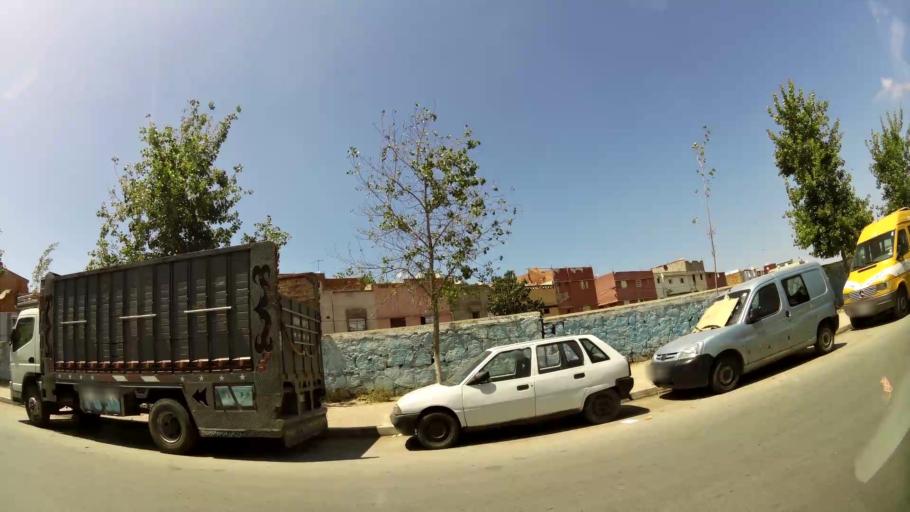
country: MA
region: Gharb-Chrarda-Beni Hssen
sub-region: Kenitra Province
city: Kenitra
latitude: 34.2523
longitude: -6.5492
